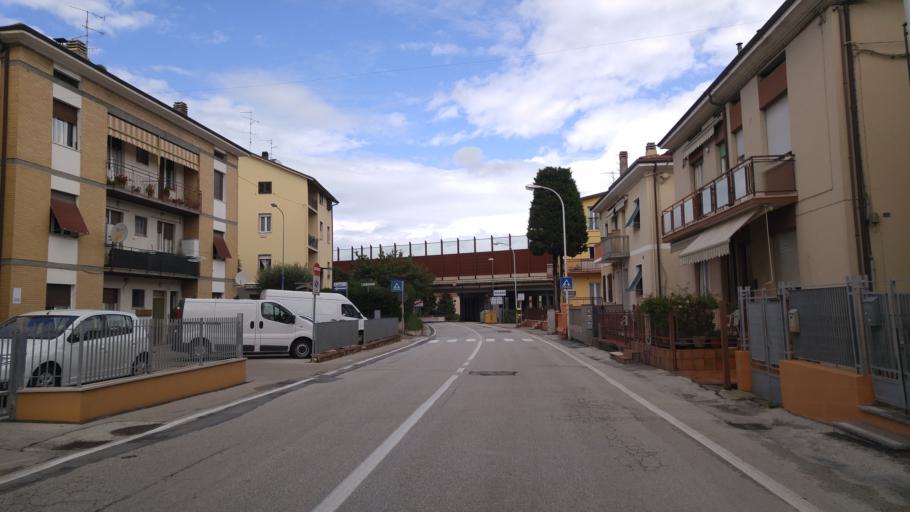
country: IT
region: The Marches
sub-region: Provincia di Pesaro e Urbino
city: Pesaro
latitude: 43.8838
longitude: 12.9018
